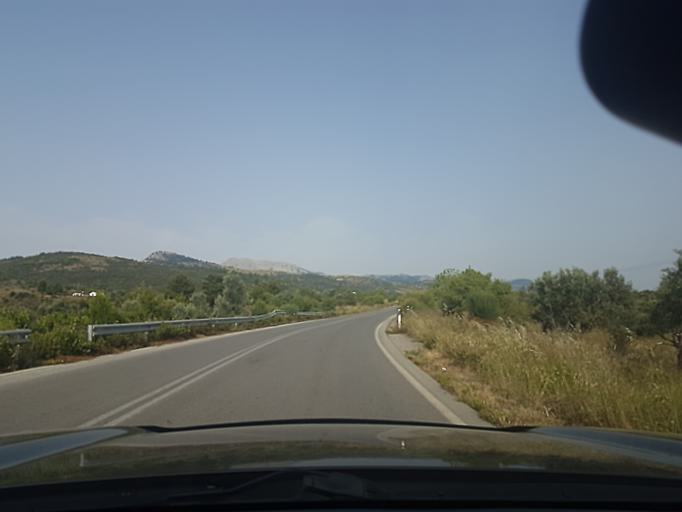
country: GR
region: Central Greece
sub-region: Nomos Evvoias
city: Yimnon
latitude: 38.5760
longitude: 23.8109
